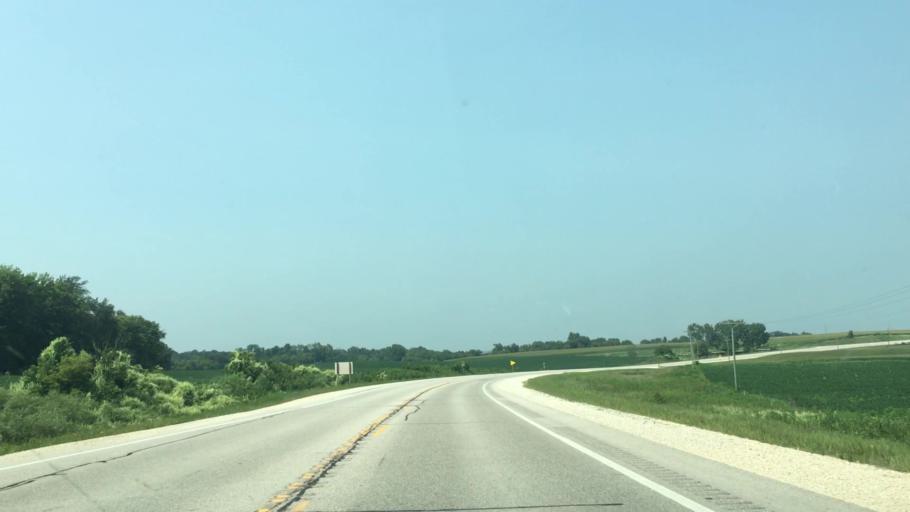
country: US
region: Iowa
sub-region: Winneshiek County
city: Decorah
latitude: 43.2066
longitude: -91.8788
